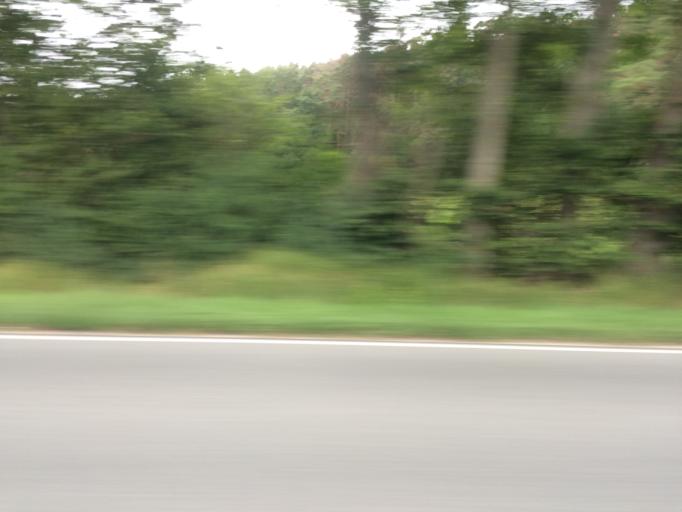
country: DE
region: Bavaria
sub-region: Regierungsbezirk Mittelfranken
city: Wilhermsdorf
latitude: 49.4870
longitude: 10.7341
